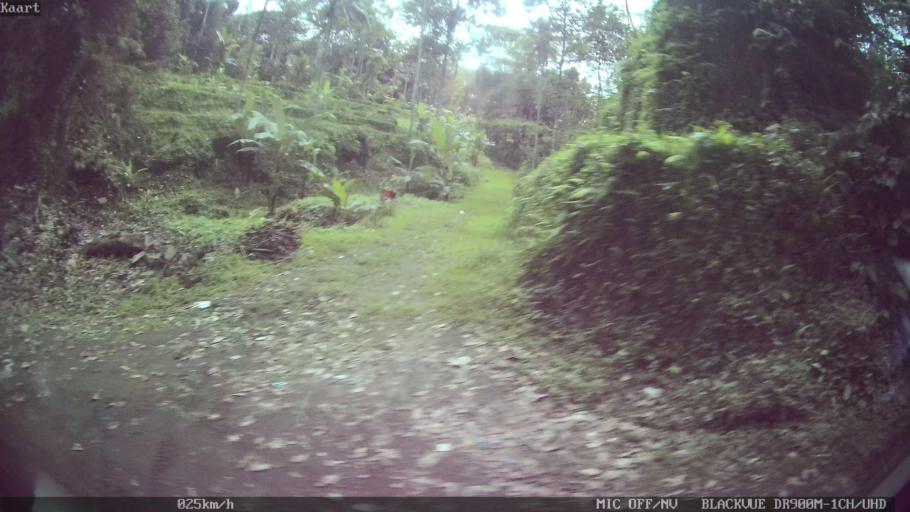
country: ID
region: Bali
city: Bangli
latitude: -8.4511
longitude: 115.3442
